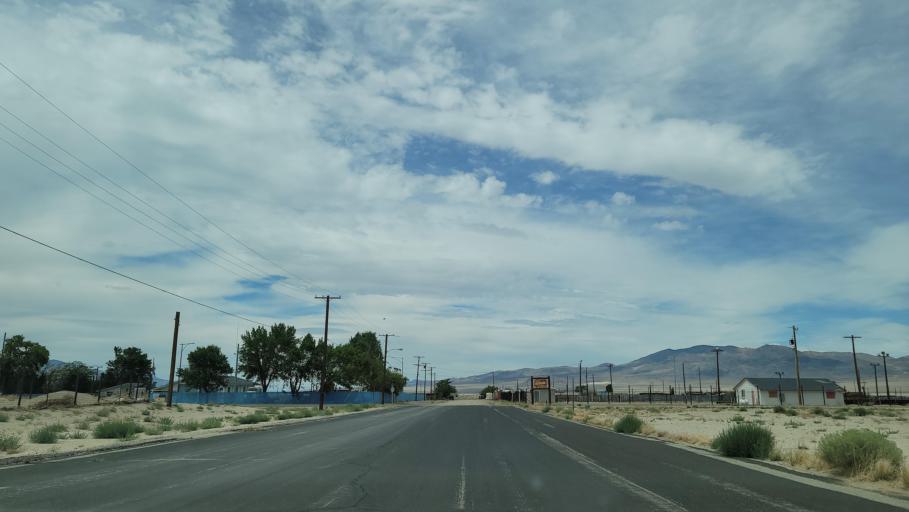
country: US
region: Nevada
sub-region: Mineral County
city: Hawthorne
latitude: 38.5283
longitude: -118.6161
